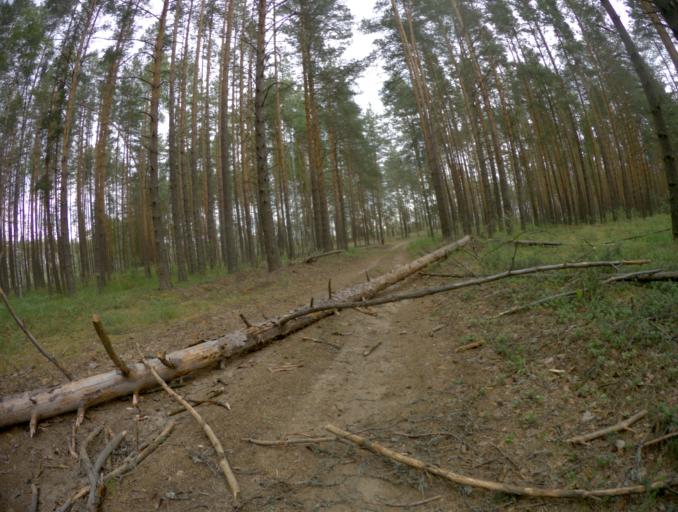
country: RU
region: Nizjnij Novgorod
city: Frolishchi
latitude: 56.3231
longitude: 42.7032
